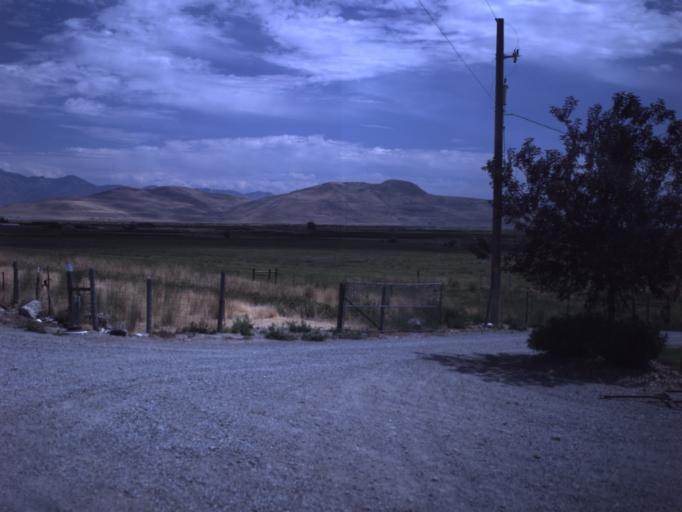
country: US
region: Utah
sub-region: Box Elder County
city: Tremonton
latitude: 41.6249
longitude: -112.3423
